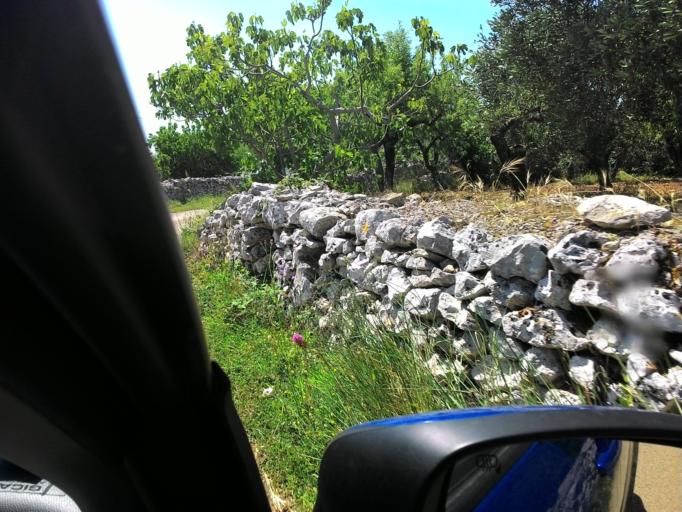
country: IT
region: Apulia
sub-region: Provincia di Bari
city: Noci
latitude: 40.8203
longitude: 17.1402
